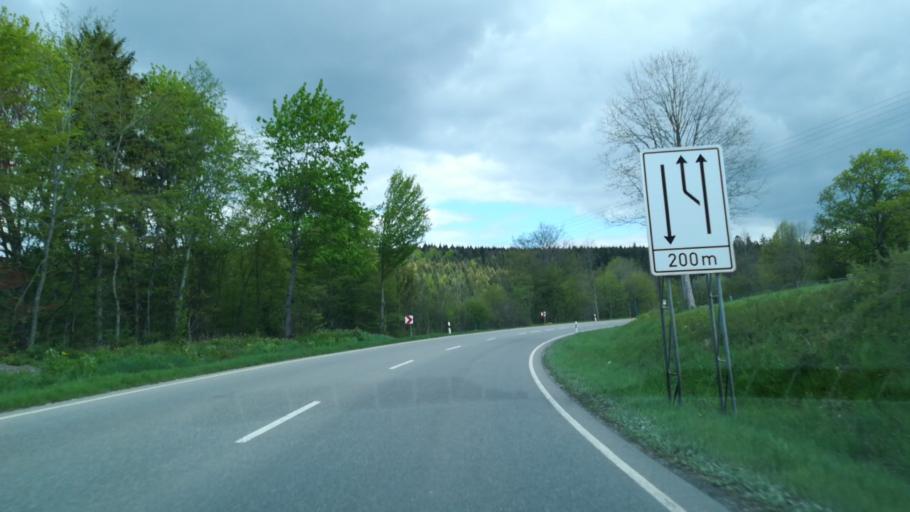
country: DE
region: Baden-Wuerttemberg
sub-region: Freiburg Region
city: Blumberg
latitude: 47.8354
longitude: 8.5615
